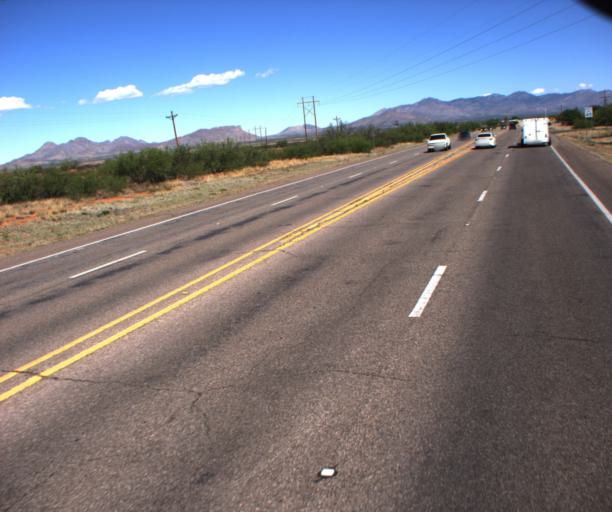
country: US
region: Arizona
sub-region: Cochise County
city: Huachuca City
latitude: 31.6154
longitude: -110.3341
